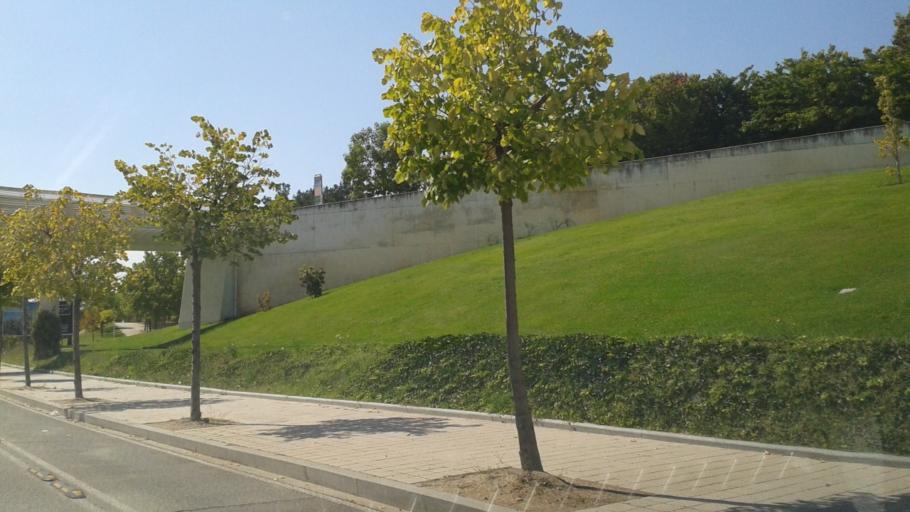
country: ES
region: Castille and Leon
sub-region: Provincia de Valladolid
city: Valladolid
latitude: 41.6375
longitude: -4.7467
